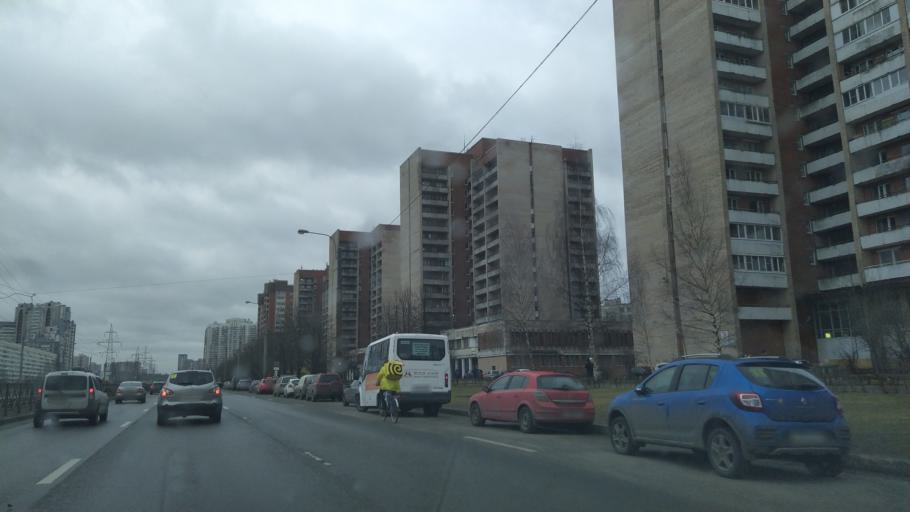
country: RU
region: St.-Petersburg
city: Komendantsky aerodrom
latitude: 60.0045
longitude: 30.2841
